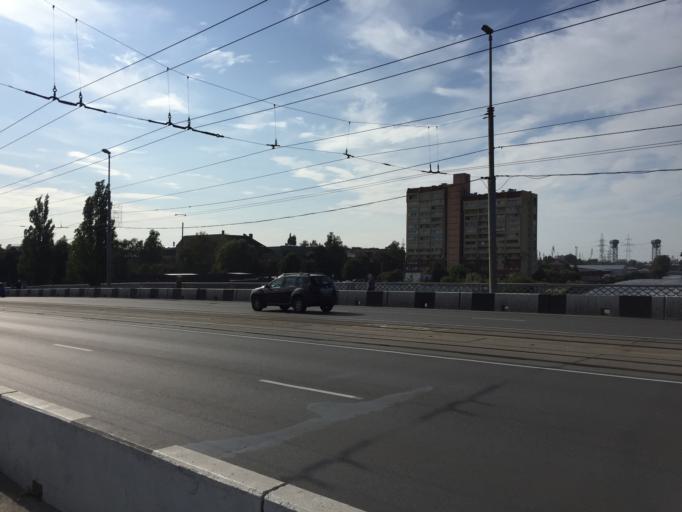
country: RU
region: Kaliningrad
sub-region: Gorod Kaliningrad
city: Kaliningrad
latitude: 54.7056
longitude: 20.5067
